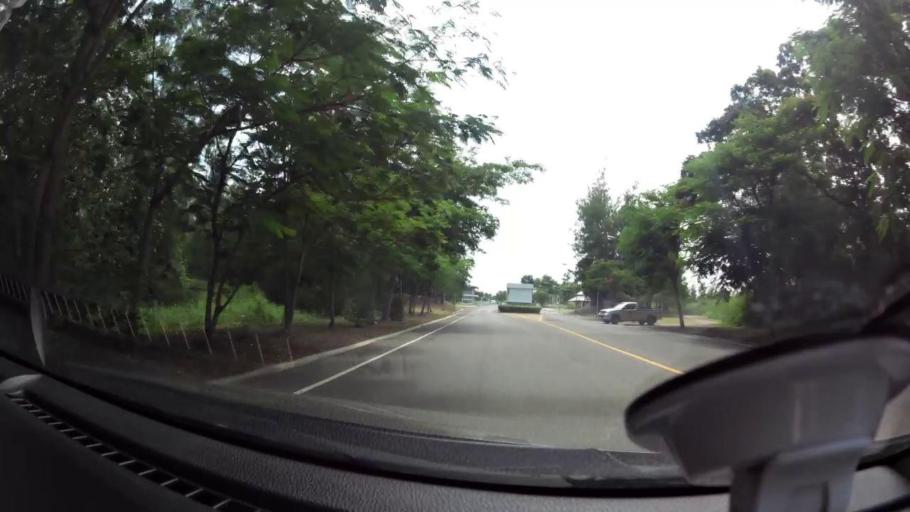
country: TH
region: Phetchaburi
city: Cha-am
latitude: 12.7059
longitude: 99.9554
